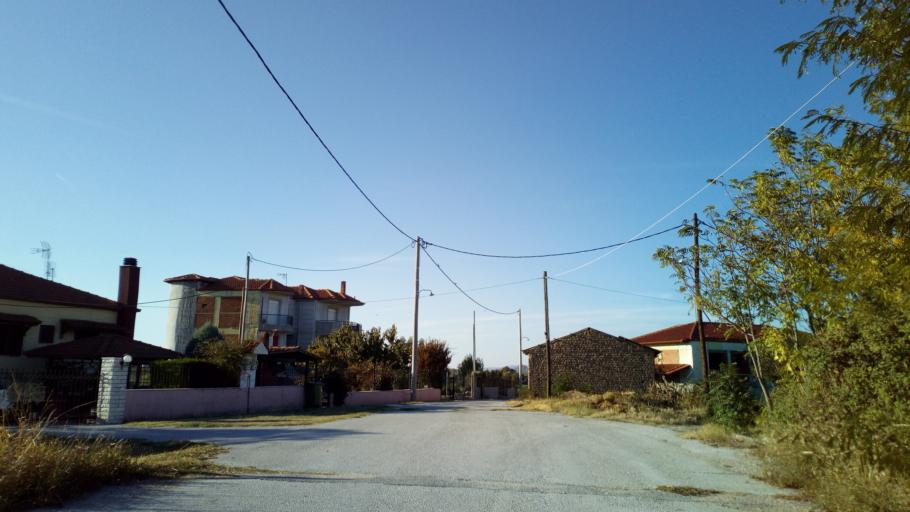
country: GR
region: Central Macedonia
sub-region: Nomos Thessalonikis
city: Gerakarou
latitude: 40.6374
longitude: 23.2429
